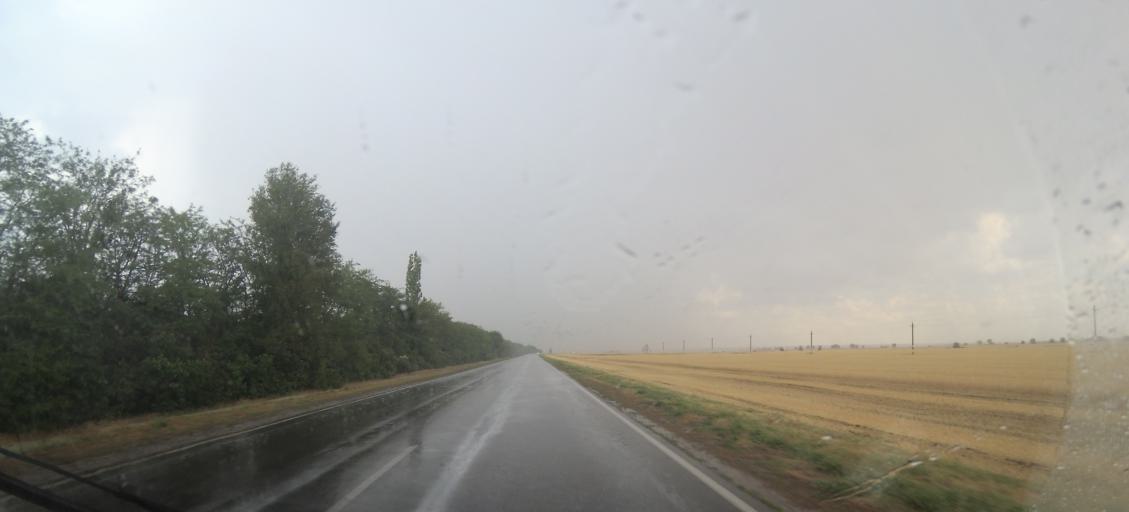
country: RU
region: Rostov
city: Proletarsk
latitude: 46.6659
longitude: 41.6893
